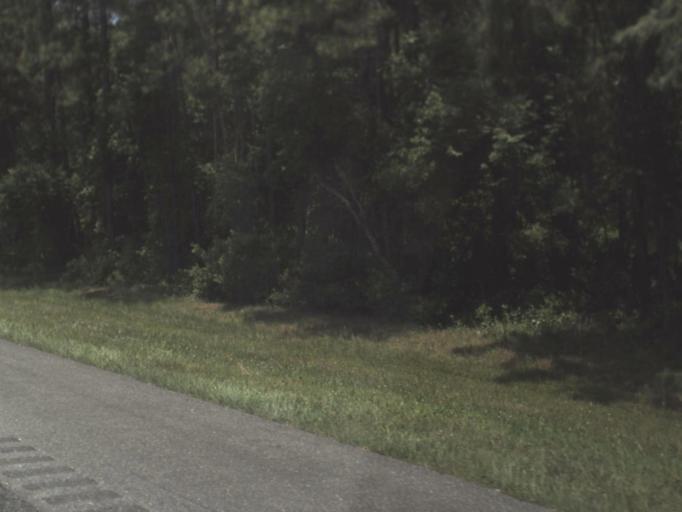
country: US
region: Florida
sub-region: Columbia County
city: Watertown
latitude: 30.2540
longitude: -82.4216
